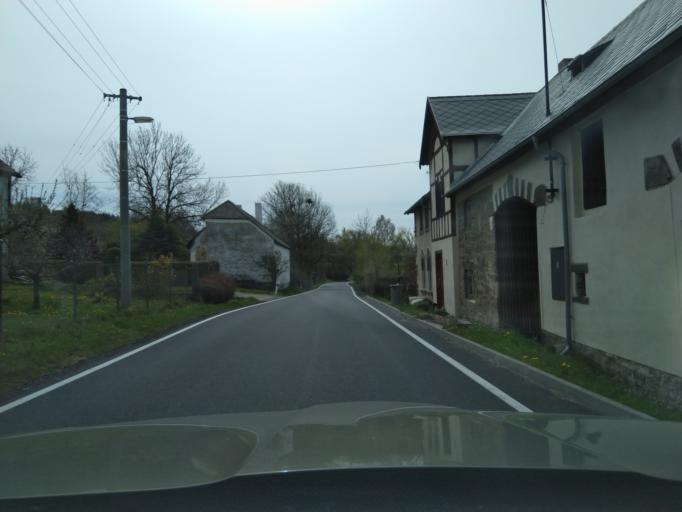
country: CZ
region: Jihocesky
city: Vacov
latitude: 49.1316
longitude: 13.7391
